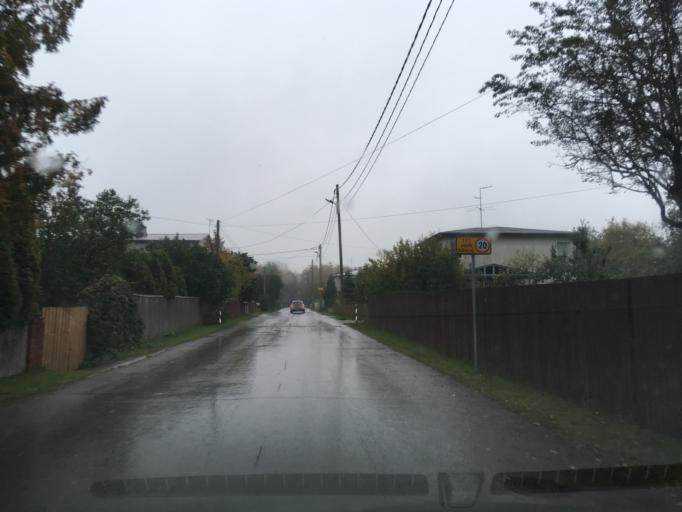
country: EE
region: Harju
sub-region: Tallinna linn
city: Kose
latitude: 59.4567
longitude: 24.8512
